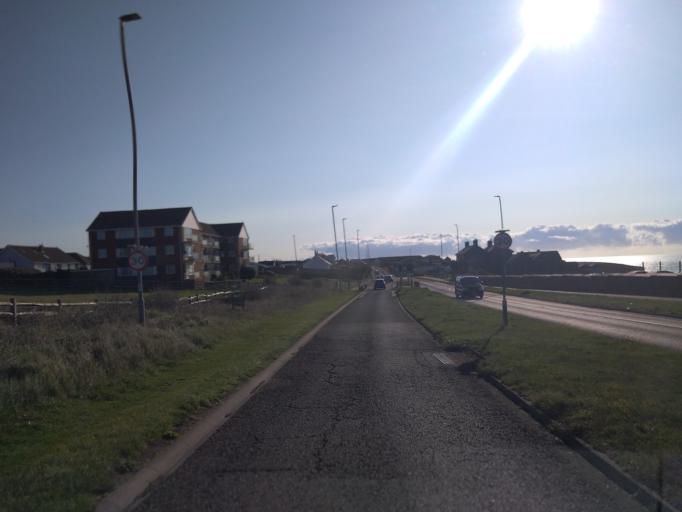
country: GB
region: England
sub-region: East Sussex
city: Peacehaven
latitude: 50.7966
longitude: -0.0242
